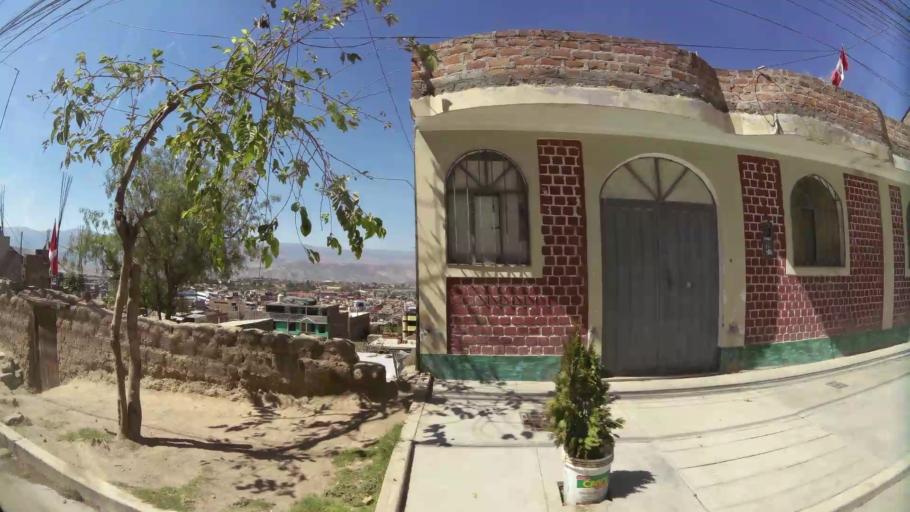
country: PE
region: Ayacucho
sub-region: Provincia de Huamanga
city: Ayacucho
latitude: -13.1499
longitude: -74.2320
